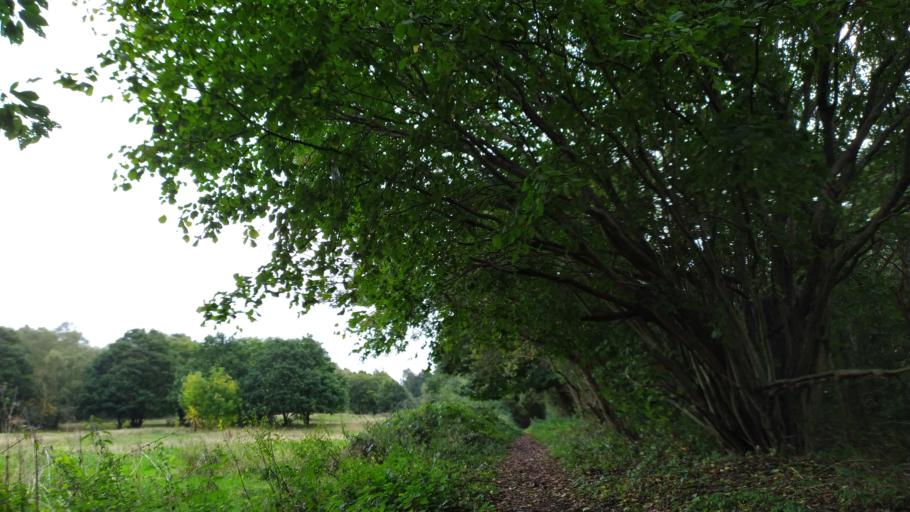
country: GB
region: England
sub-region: City and Borough of Leeds
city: Chapel Allerton
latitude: 53.8218
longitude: -1.5537
